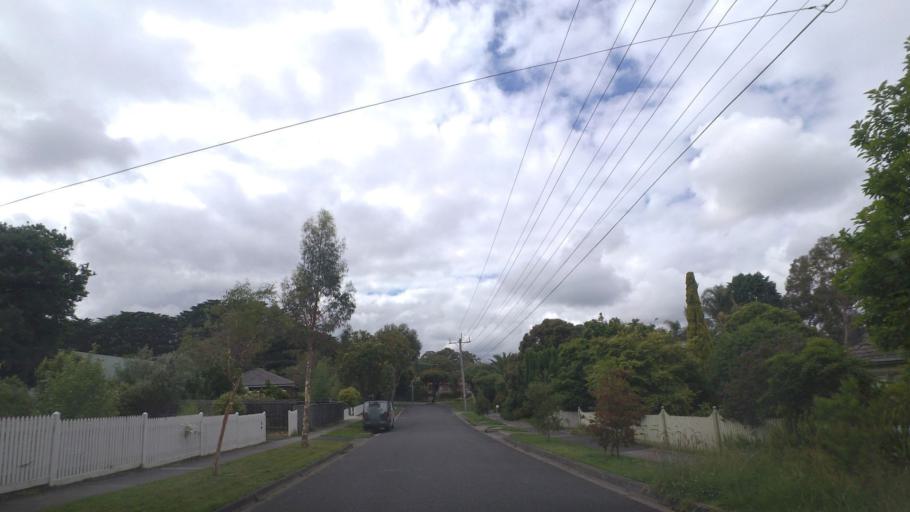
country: AU
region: Victoria
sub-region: Maroondah
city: Croydon South
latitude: -37.7984
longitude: 145.2676
